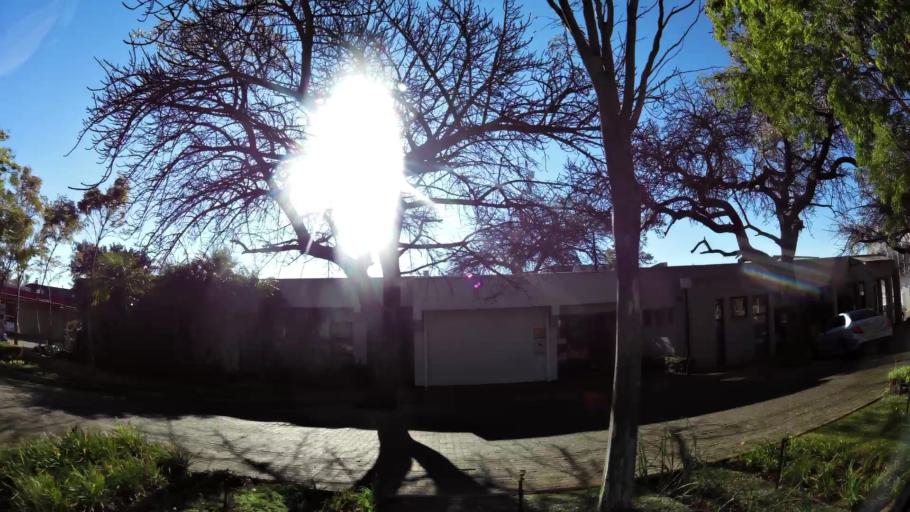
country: ZA
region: Limpopo
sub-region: Capricorn District Municipality
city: Polokwane
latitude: -23.8968
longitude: 29.4796
